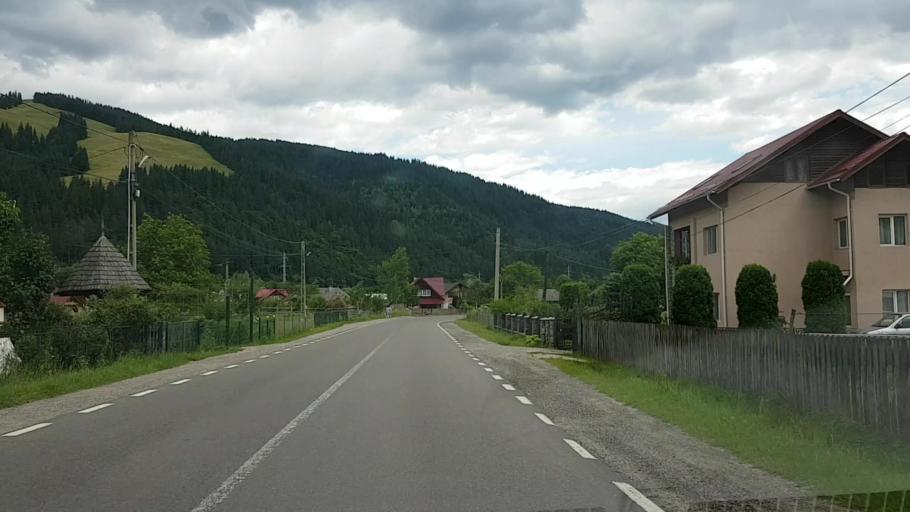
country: RO
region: Neamt
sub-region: Comuna Poiana Teiului
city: Poiana Teiului
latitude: 47.1119
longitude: 25.9304
